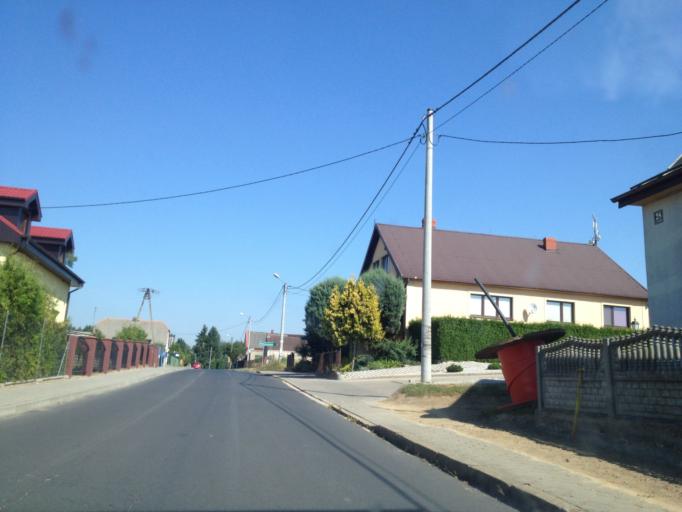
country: PL
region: Greater Poland Voivodeship
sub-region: Powiat sredzki
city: Zaniemysl
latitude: 52.1169
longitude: 17.1164
